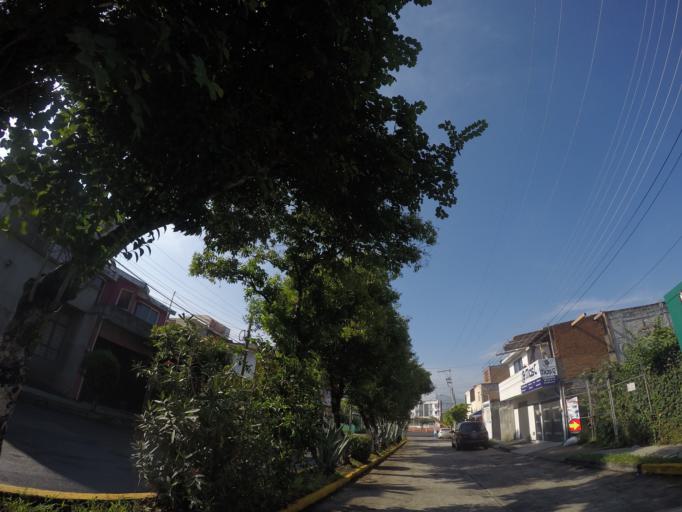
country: MX
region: Michoacan
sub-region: Morelia
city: Morelos
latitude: 19.6751
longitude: -101.2144
